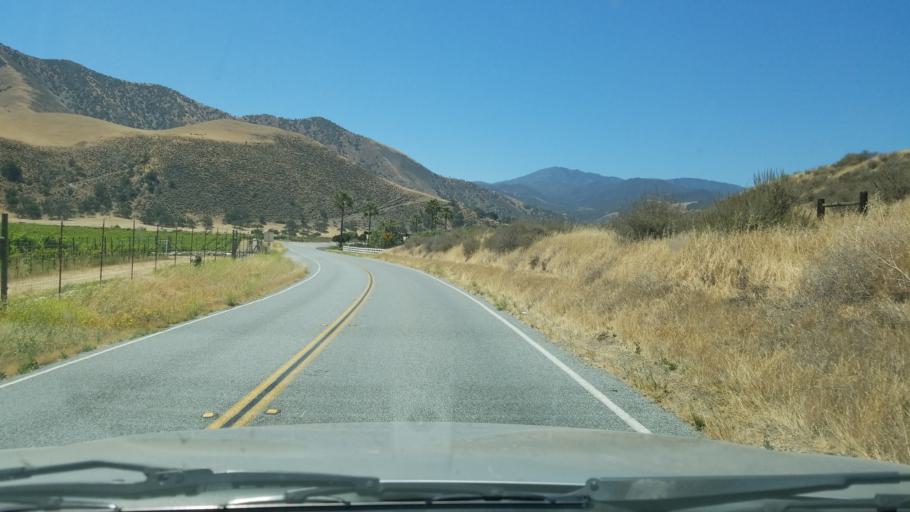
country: US
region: California
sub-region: Monterey County
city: Greenfield
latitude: 36.2848
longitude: -121.3206
